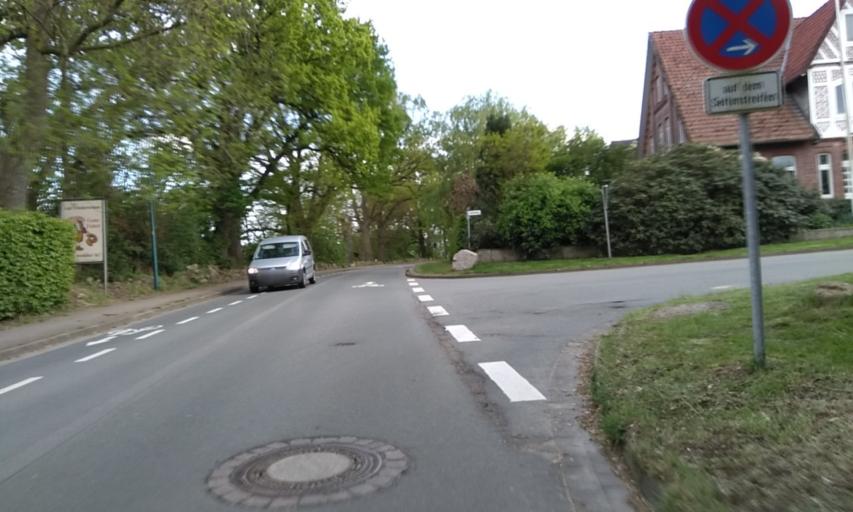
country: DE
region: Lower Saxony
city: Buxtehude
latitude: 53.4473
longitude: 9.6667
